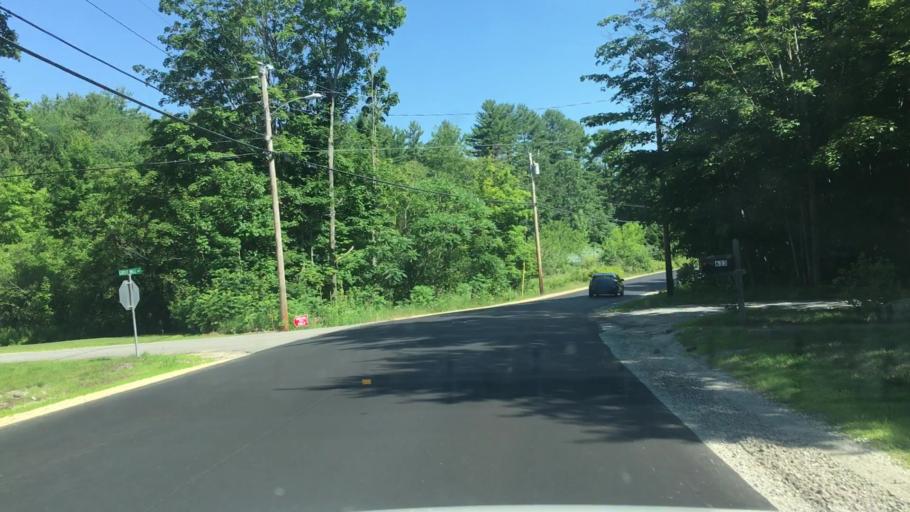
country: US
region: Maine
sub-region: Cumberland County
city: Cumberland Center
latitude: 43.8016
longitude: -70.3289
